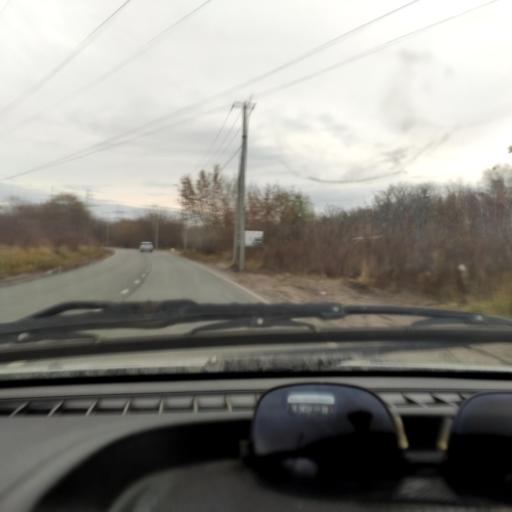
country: RU
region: Samara
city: Zhigulevsk
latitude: 53.5123
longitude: 49.4676
